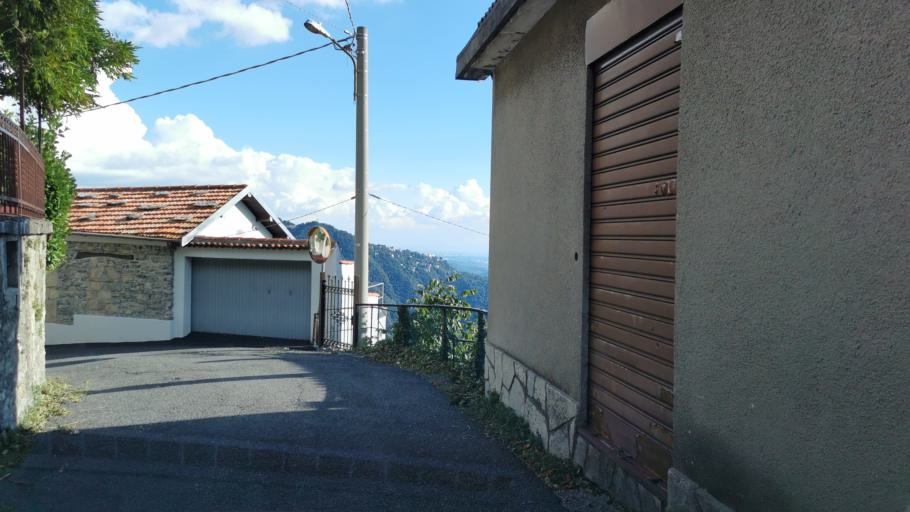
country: IT
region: Lombardy
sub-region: Provincia di Como
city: Cernobbio
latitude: 45.8581
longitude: 9.0727
